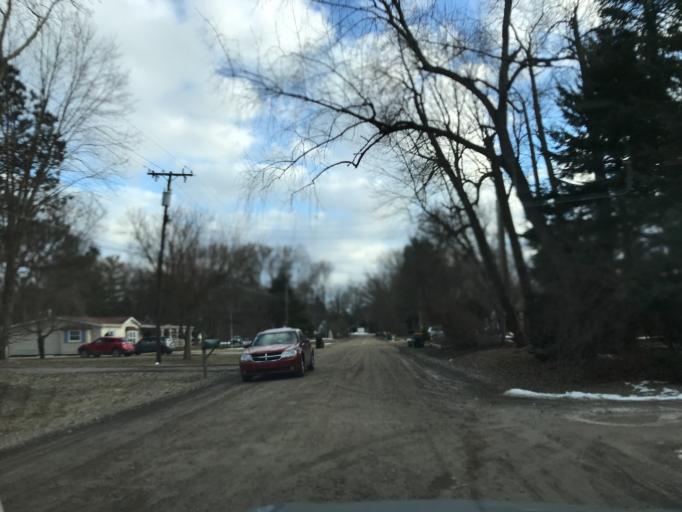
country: US
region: Michigan
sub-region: Oakland County
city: Farmington
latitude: 42.4546
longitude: -83.3272
